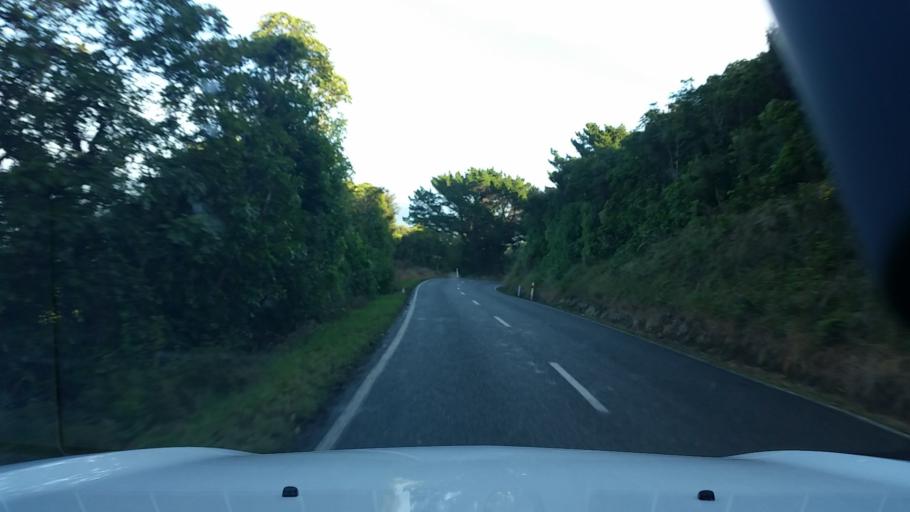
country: NZ
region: Wellington
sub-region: South Wairarapa District
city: Waipawa
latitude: -41.4379
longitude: 175.2240
